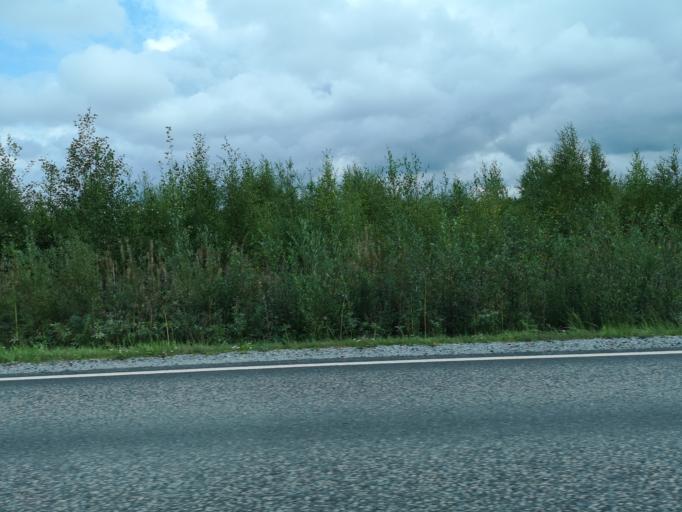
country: FI
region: Central Finland
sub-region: Jyvaeskylae
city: Hankasalmi
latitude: 62.3683
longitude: 26.4461
